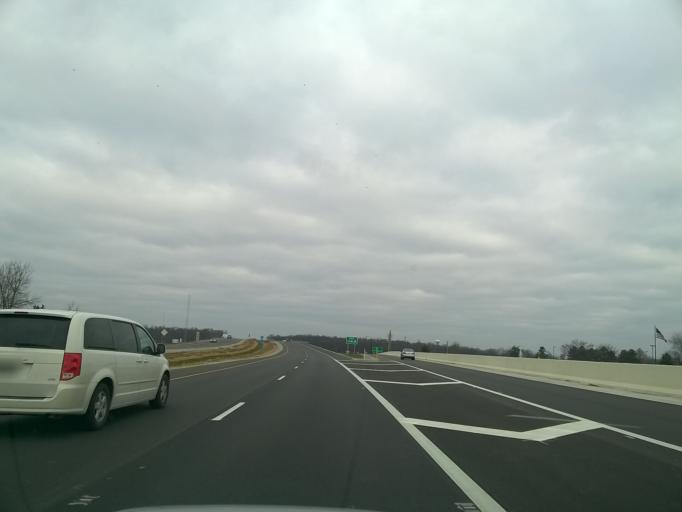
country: US
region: Indiana
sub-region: Hamilton County
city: Westfield
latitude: 40.0625
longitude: -86.1278
